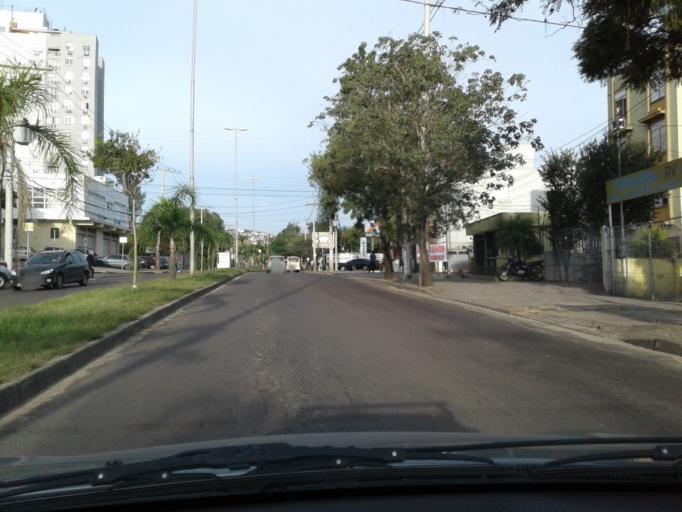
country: BR
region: Rio Grande do Sul
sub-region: Porto Alegre
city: Porto Alegre
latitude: -30.0920
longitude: -51.2413
